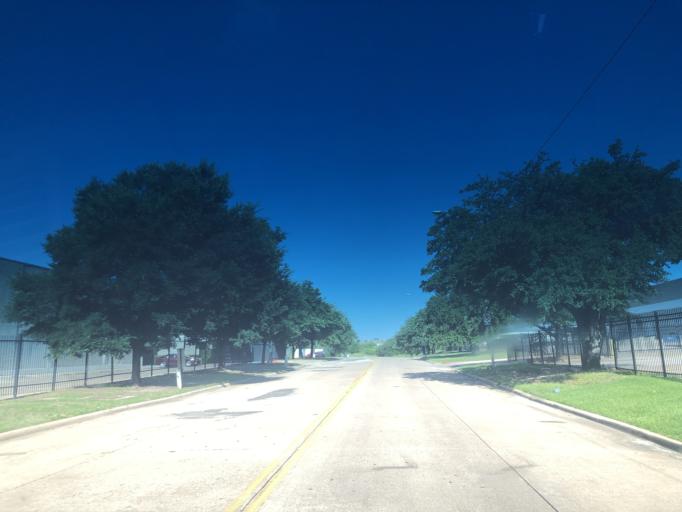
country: US
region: Texas
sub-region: Dallas County
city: Grand Prairie
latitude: 32.7293
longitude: -97.0423
